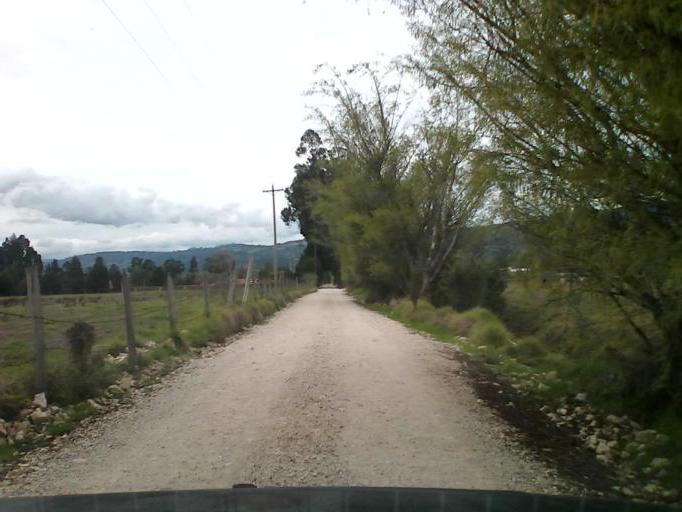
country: CO
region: Boyaca
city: Duitama
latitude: 5.7851
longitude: -73.0521
